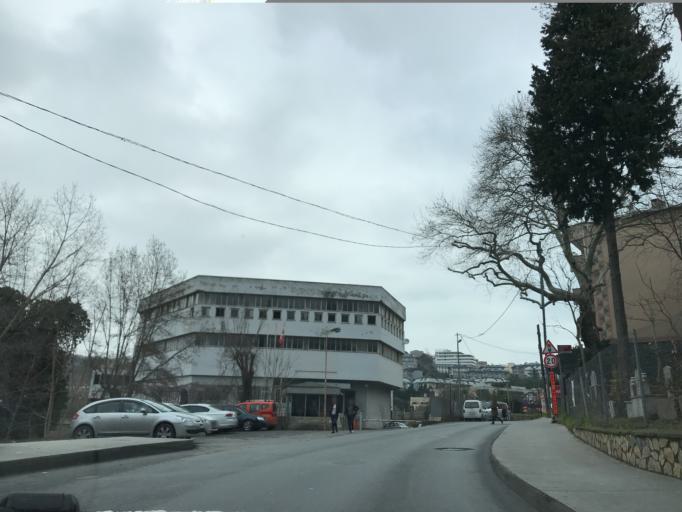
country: TR
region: Istanbul
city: Sisli
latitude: 41.1175
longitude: 29.0503
